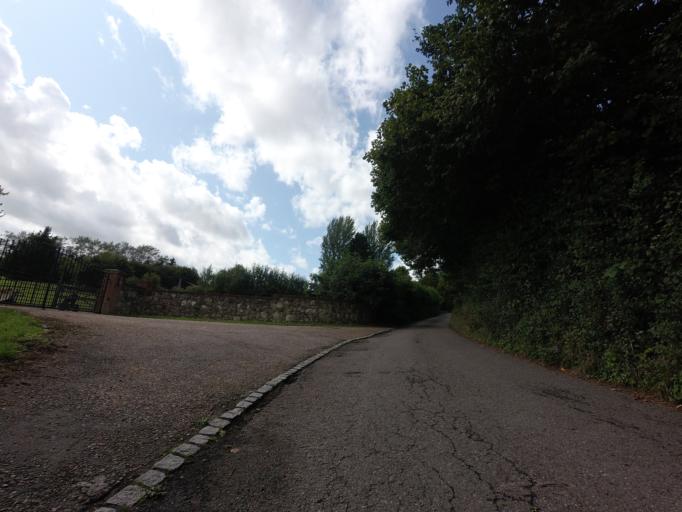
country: GB
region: England
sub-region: Kent
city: Borough Green
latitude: 51.2622
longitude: 0.3026
